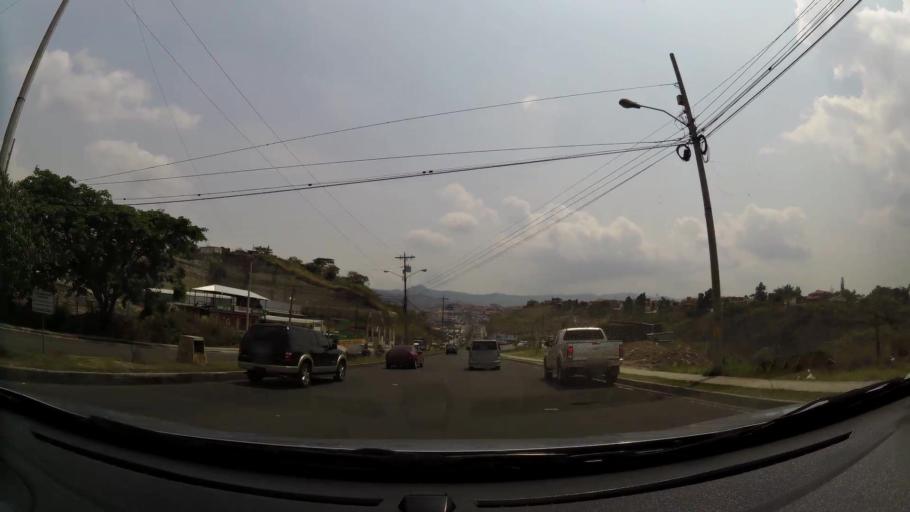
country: HN
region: Francisco Morazan
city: Yaguacire
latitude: 14.0446
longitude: -87.2259
